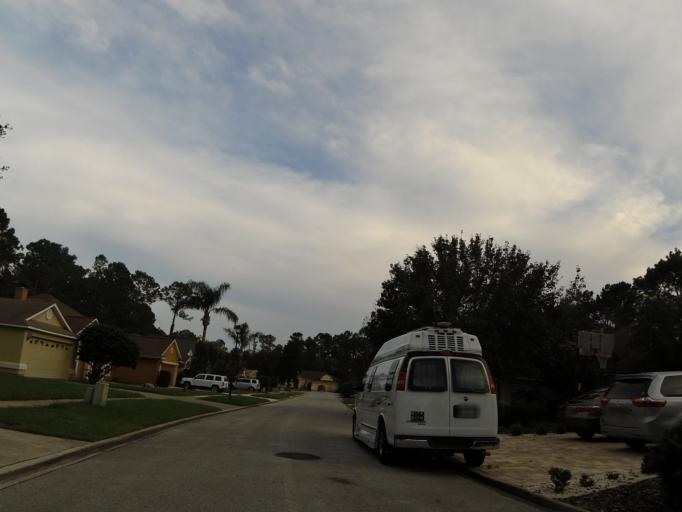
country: US
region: Florida
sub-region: Saint Johns County
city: Palm Valley
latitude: 30.2076
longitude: -81.5185
